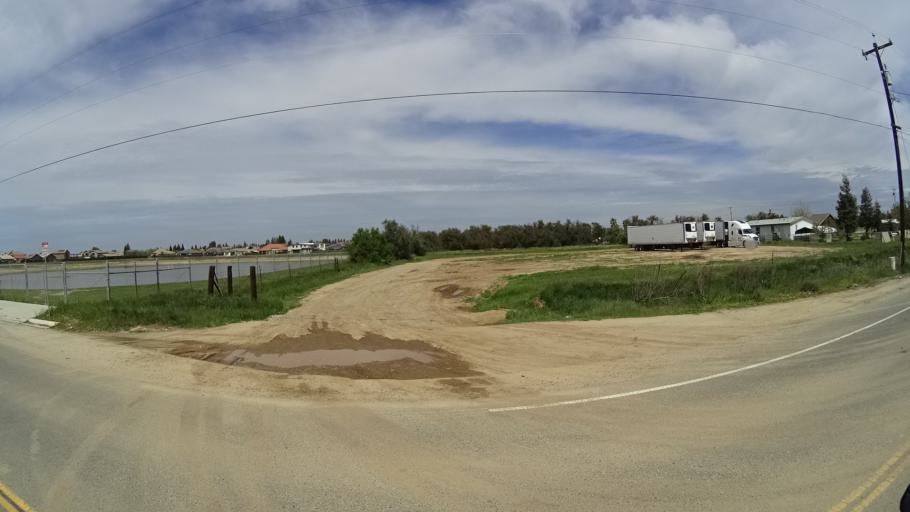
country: US
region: California
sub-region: Fresno County
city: Biola
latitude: 36.8151
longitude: -119.9178
